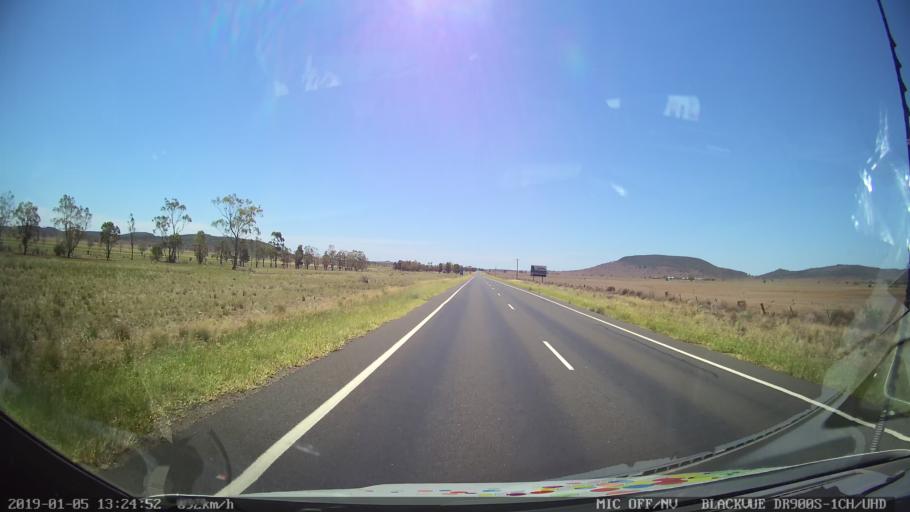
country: AU
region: New South Wales
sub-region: Gunnedah
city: Gunnedah
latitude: -31.0658
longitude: 149.9947
